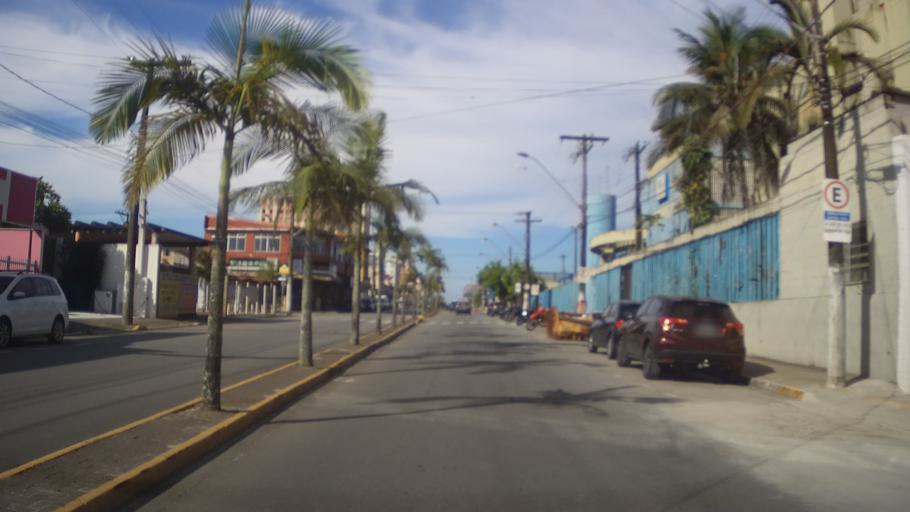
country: BR
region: Sao Paulo
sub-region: Itanhaem
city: Itanhaem
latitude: -24.1859
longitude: -46.7900
